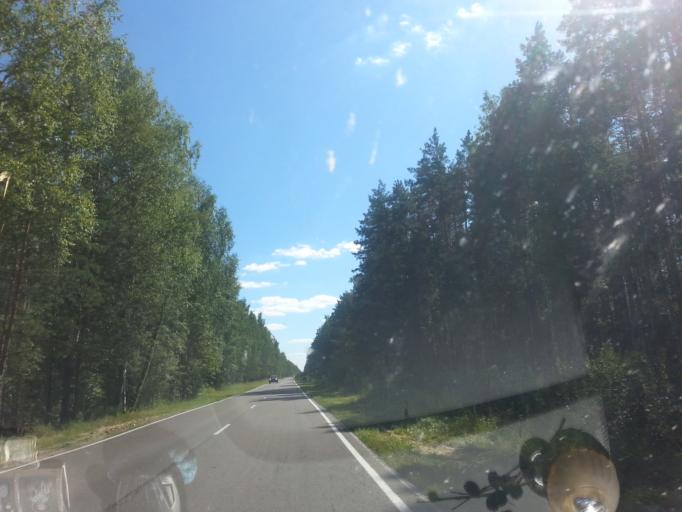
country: RU
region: Vladimir
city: Galitsy
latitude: 56.0631
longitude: 42.8660
